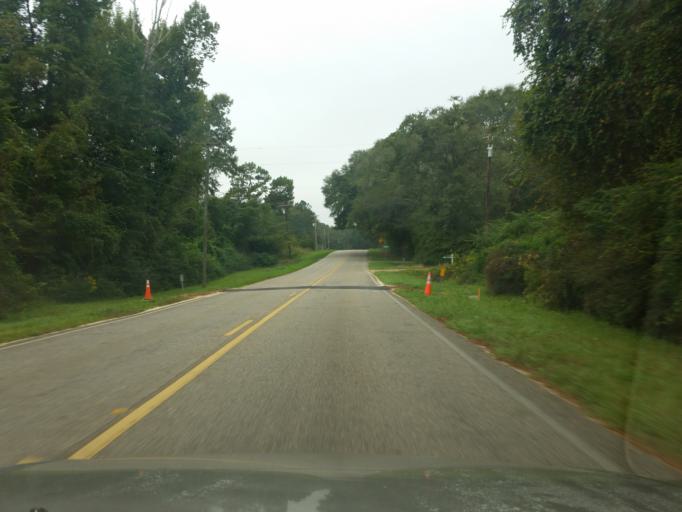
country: US
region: Alabama
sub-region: Baldwin County
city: Bay Minette
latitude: 30.8470
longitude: -87.8305
